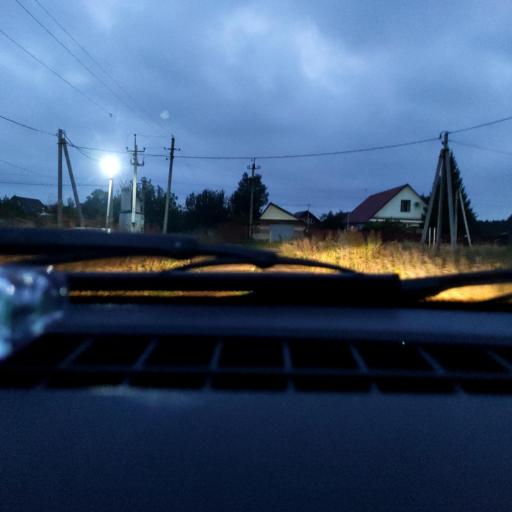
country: RU
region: Bashkortostan
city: Iglino
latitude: 54.7304
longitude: 56.3280
